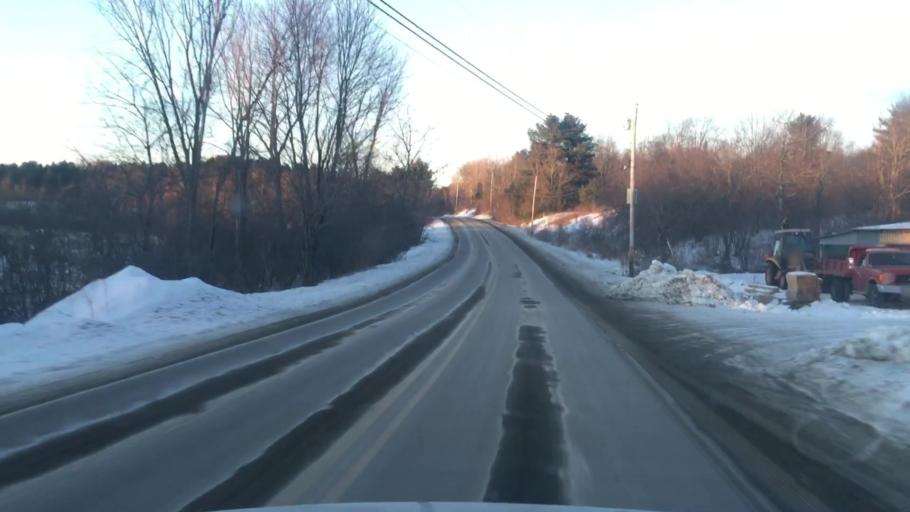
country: US
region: Maine
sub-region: Penobscot County
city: Brewer
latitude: 44.7390
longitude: -68.7652
